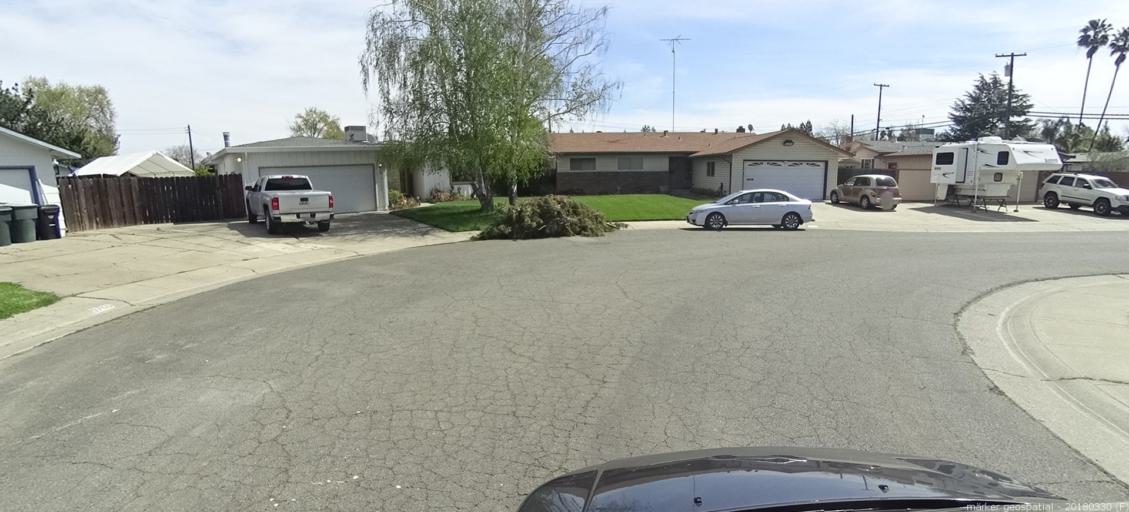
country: US
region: California
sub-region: Sacramento County
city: Rosemont
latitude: 38.5463
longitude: -121.3645
